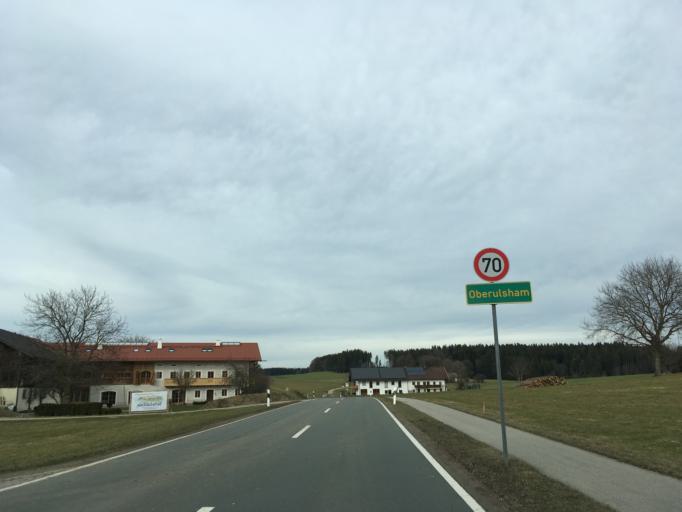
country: DE
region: Bavaria
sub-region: Upper Bavaria
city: Eggstatt
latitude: 47.9410
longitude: 12.3573
